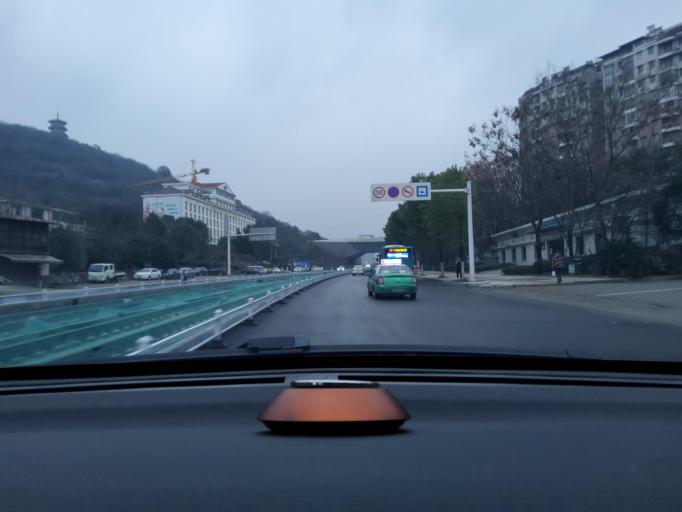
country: CN
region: Hubei
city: Tuanchengshan
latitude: 30.1950
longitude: 115.0201
